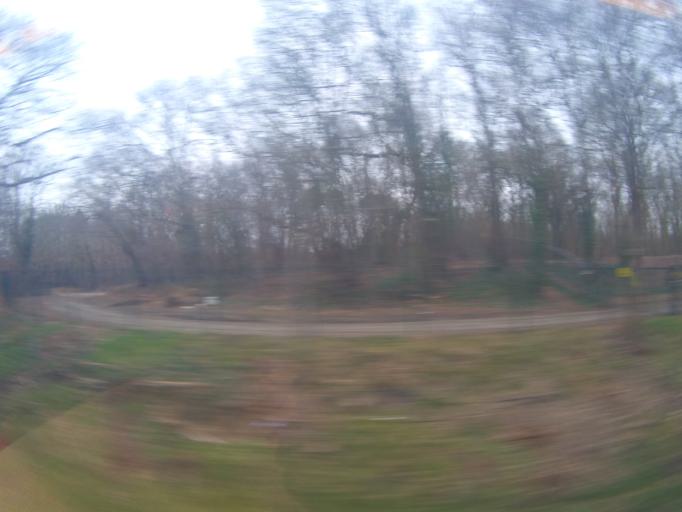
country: NL
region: Utrecht
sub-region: Gemeente Amersfoort
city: Amersfoort
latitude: 52.1511
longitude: 5.3548
